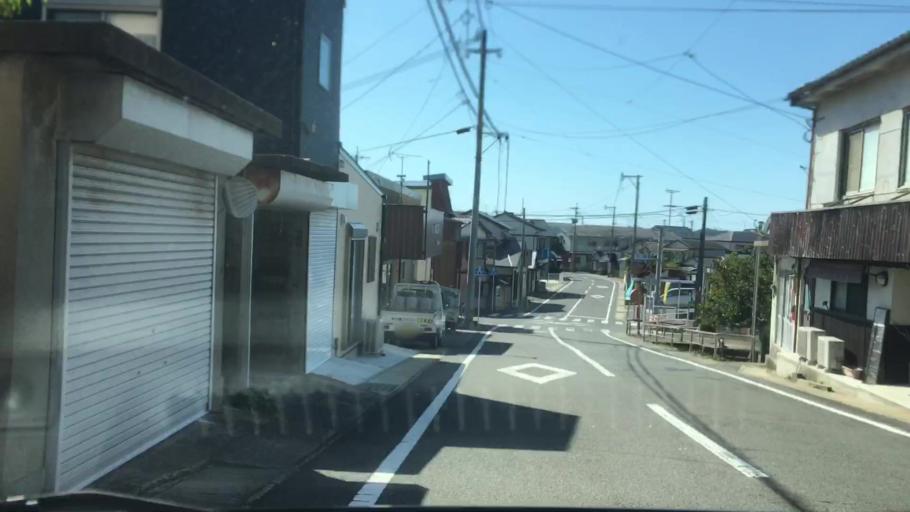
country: JP
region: Nagasaki
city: Sasebo
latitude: 33.0371
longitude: 129.6191
